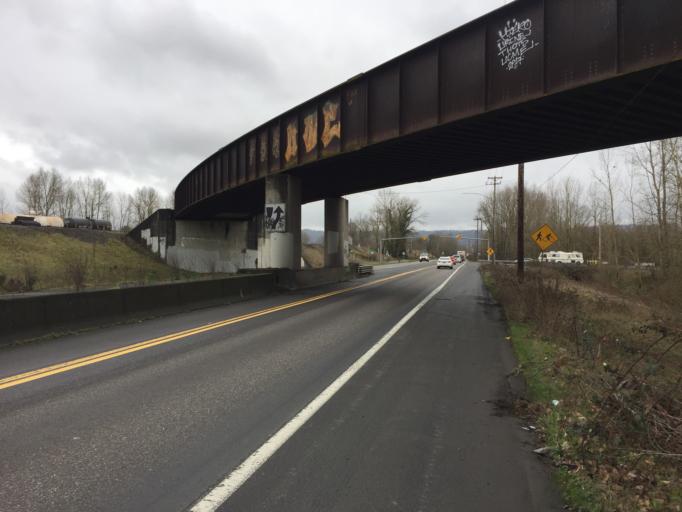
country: US
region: Washington
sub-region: Clark County
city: Vancouver
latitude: 45.6088
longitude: -122.7095
